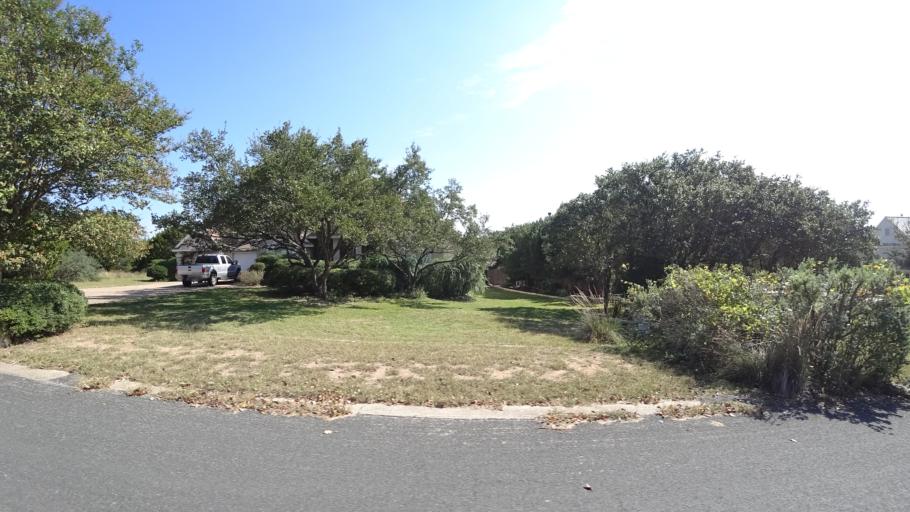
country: US
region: Texas
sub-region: Travis County
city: Bee Cave
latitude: 30.2285
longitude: -97.9359
